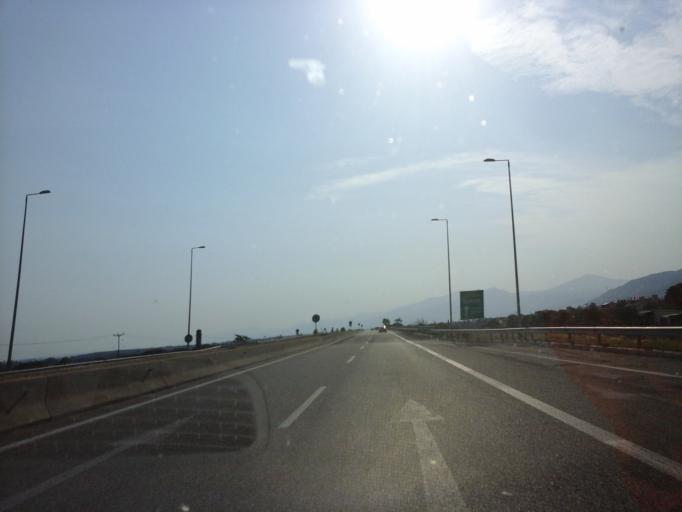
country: GR
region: East Macedonia and Thrace
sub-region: Nomos Xanthis
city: Selero
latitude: 41.1205
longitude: 25.0731
